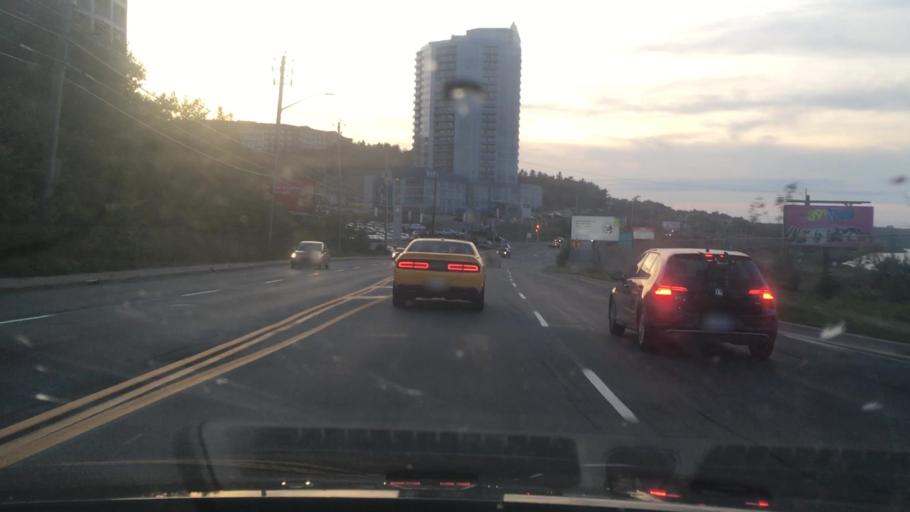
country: CA
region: Nova Scotia
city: Dartmouth
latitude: 44.6632
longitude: -63.6319
